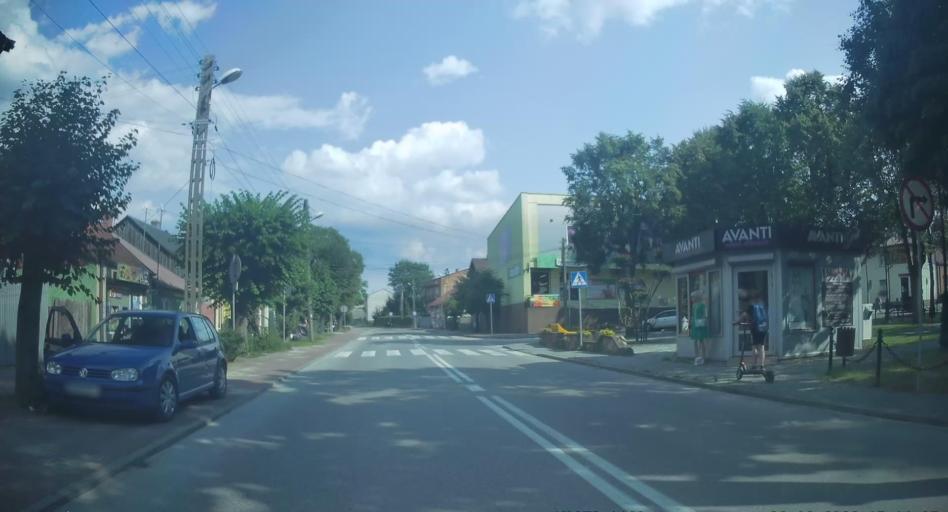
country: PL
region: Swietokrzyskie
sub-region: Powiat konecki
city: Radoszyce
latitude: 51.0738
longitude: 20.2604
